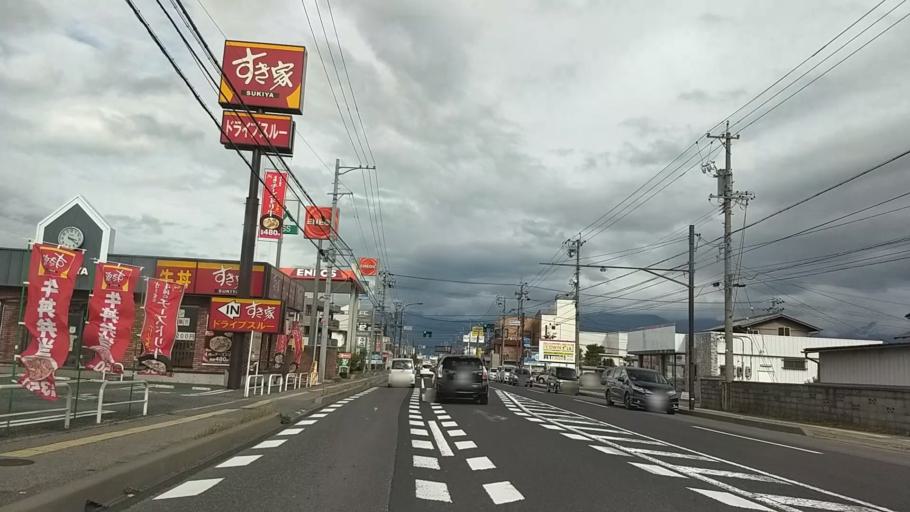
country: JP
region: Nagano
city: Nagano-shi
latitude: 36.6554
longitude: 138.2395
